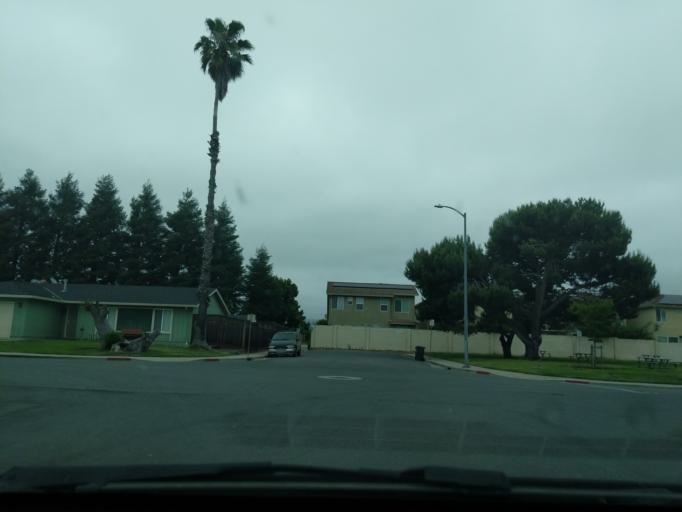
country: US
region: California
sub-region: Santa Cruz County
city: Watsonville
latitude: 36.9244
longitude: -121.7415
